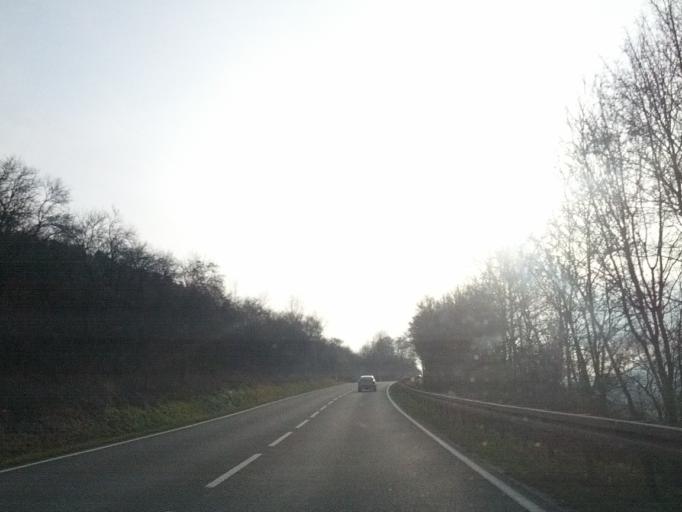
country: DE
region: Thuringia
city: Walldorf
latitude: 50.6136
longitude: 10.4014
